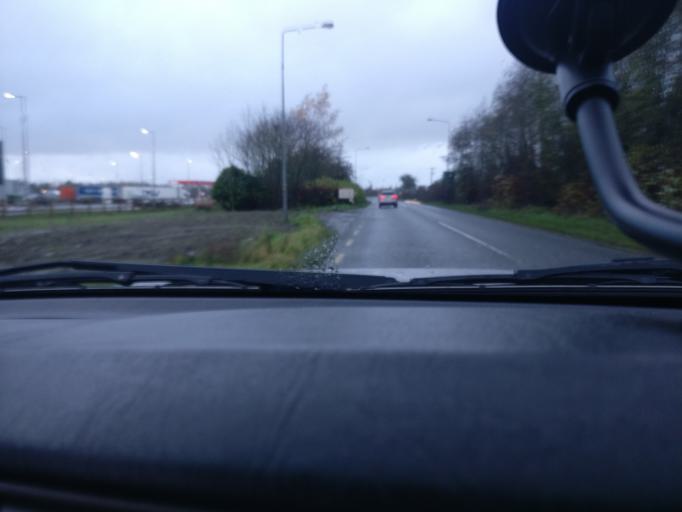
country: IE
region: Leinster
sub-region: An Iarmhi
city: Kinnegad
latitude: 53.4528
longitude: -7.1067
